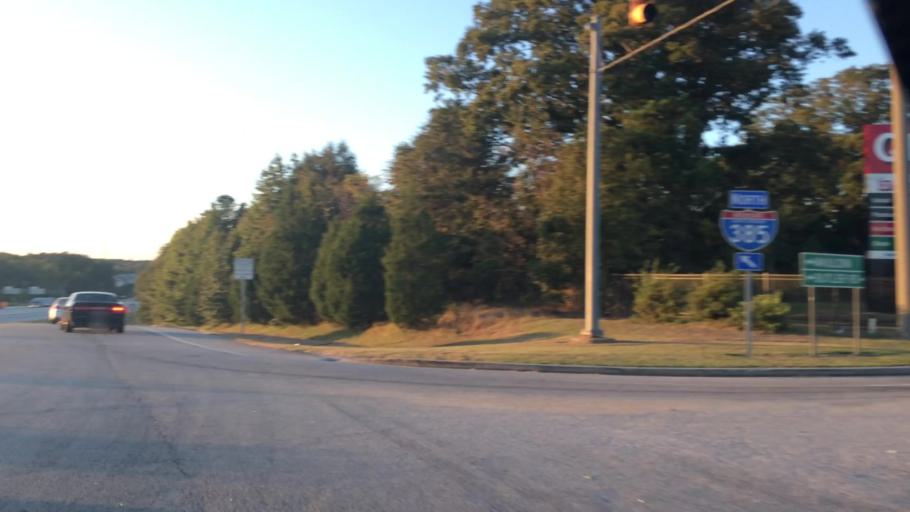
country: US
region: South Carolina
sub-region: Greenville County
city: Mauldin
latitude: 34.8067
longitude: -82.2825
